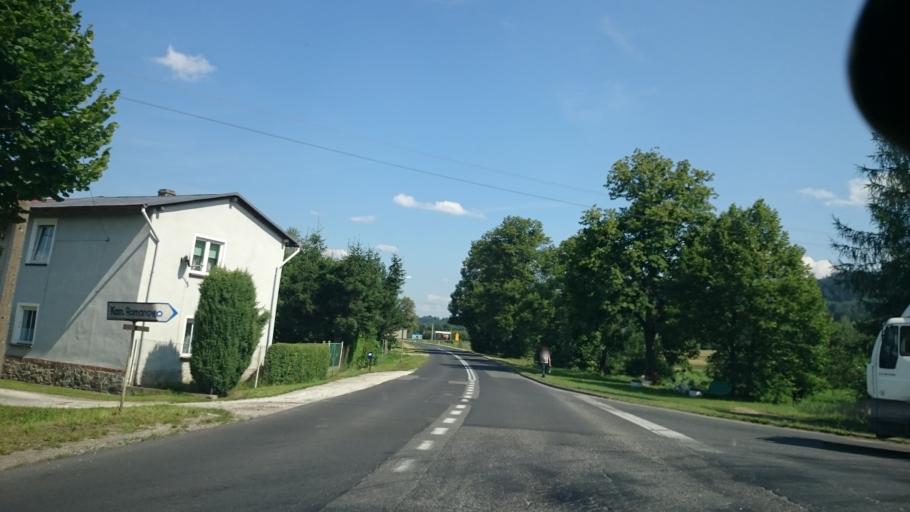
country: PL
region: Lower Silesian Voivodeship
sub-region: Powiat klodzki
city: Ladek-Zdroj
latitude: 50.3480
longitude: 16.7657
